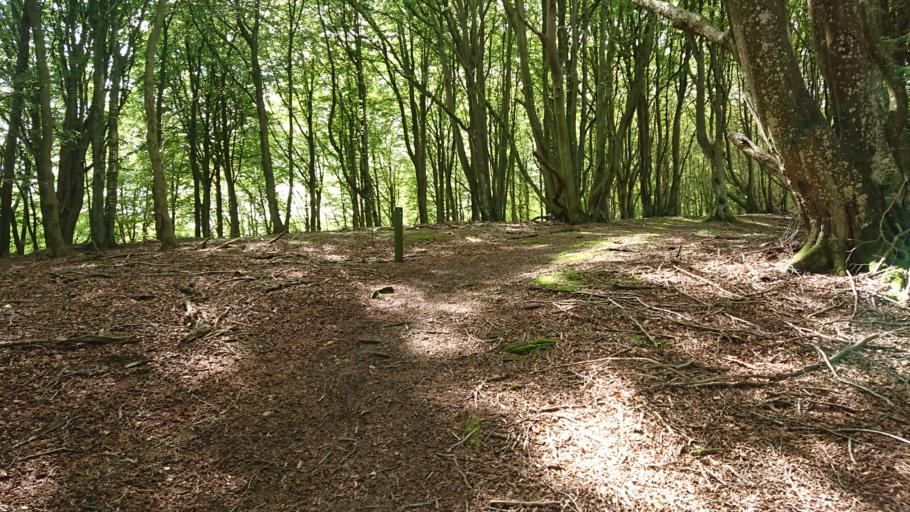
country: DK
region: North Denmark
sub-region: Hjorring Kommune
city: Sindal
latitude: 57.4512
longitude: 10.3329
